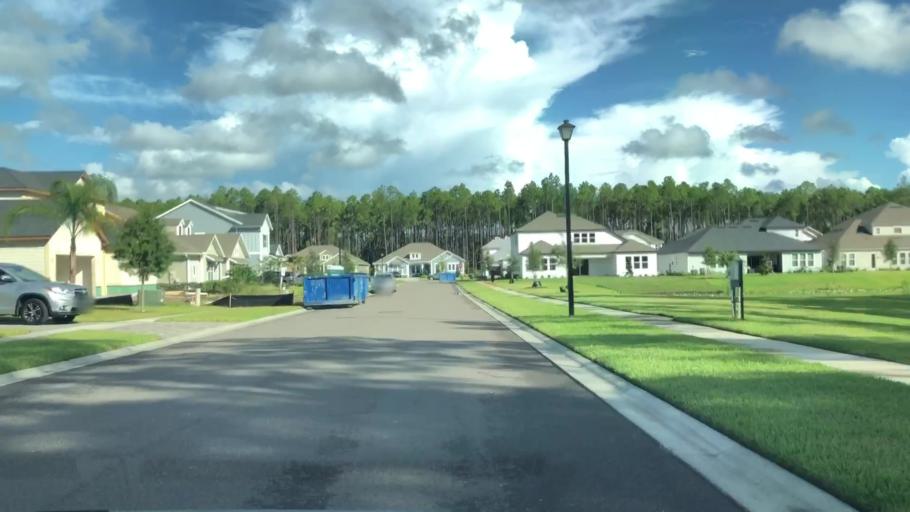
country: US
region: Florida
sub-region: Saint Johns County
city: Palm Valley
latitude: 30.1402
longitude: -81.4111
